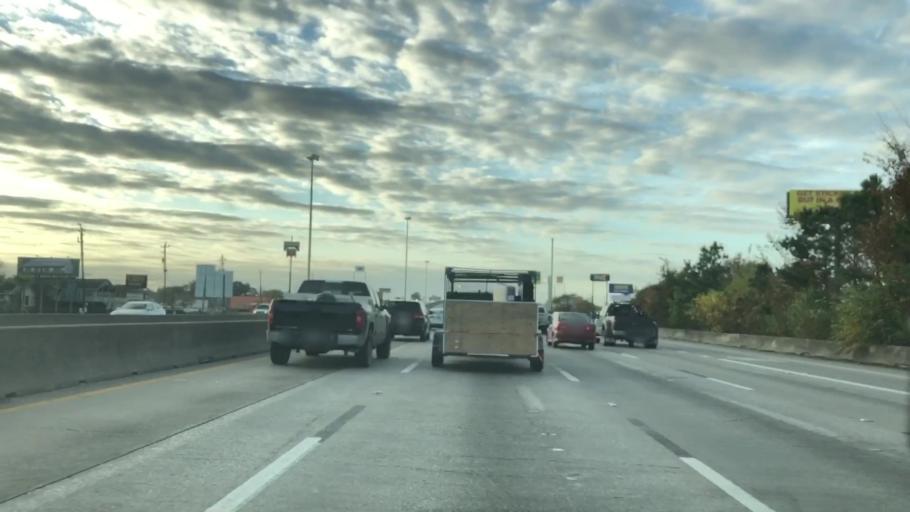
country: US
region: Texas
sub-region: Harris County
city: Aldine
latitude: 29.9017
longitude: -95.4125
